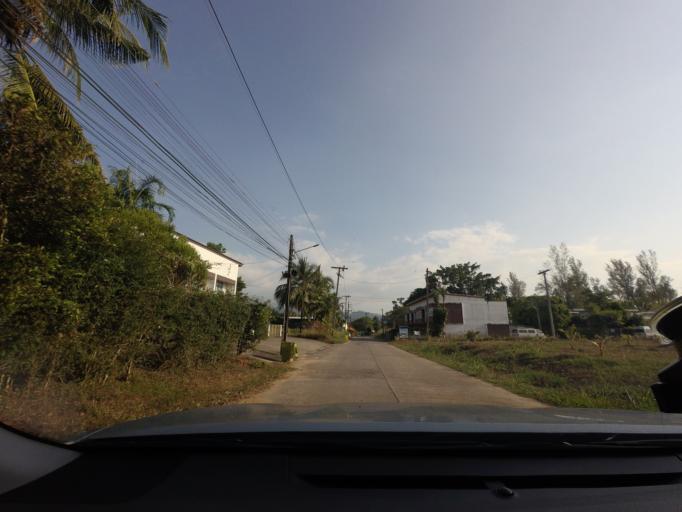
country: TH
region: Phangnga
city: Ban Khao Lak
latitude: 8.6952
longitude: 98.2510
